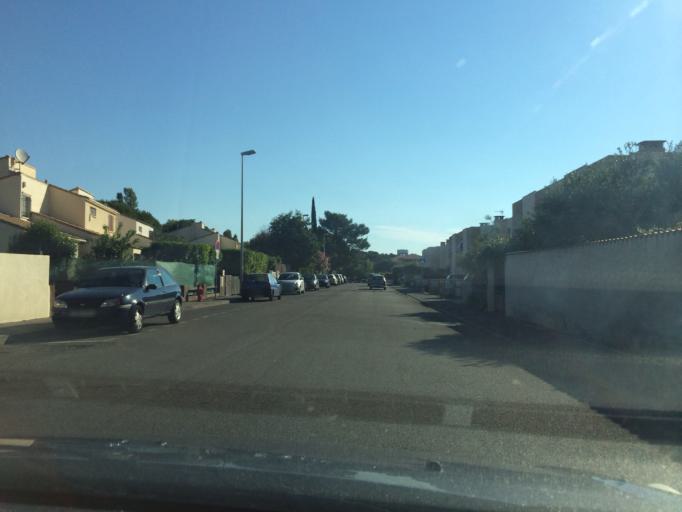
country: FR
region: Languedoc-Roussillon
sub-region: Departement de l'Herault
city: Juvignac
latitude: 43.6282
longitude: 3.8421
